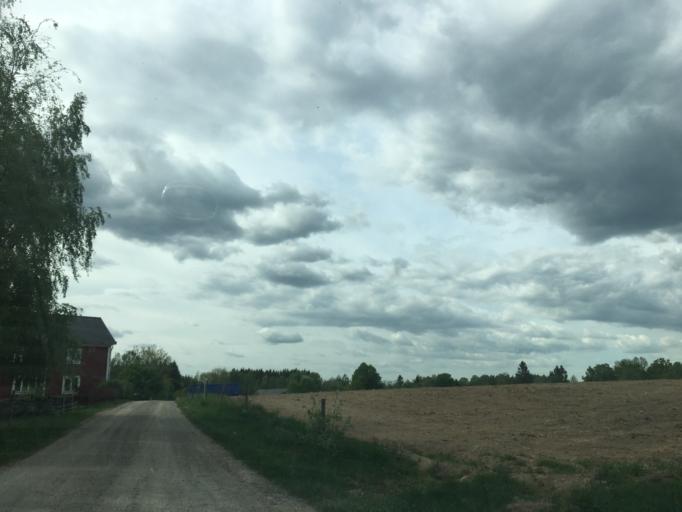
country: SE
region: Blekinge
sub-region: Olofstroms Kommun
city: Olofstroem
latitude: 56.4007
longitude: 14.5840
